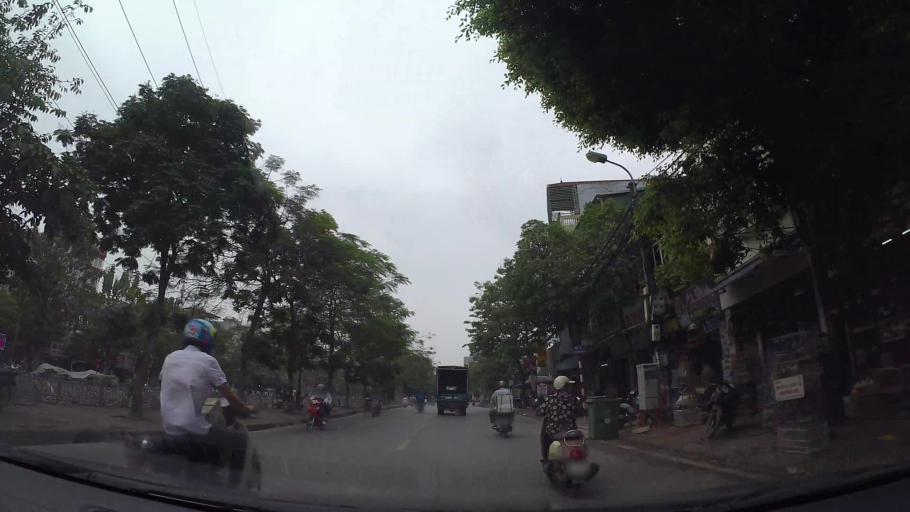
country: VN
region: Ha Noi
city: Hai BaTrung
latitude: 21.0065
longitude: 105.8610
